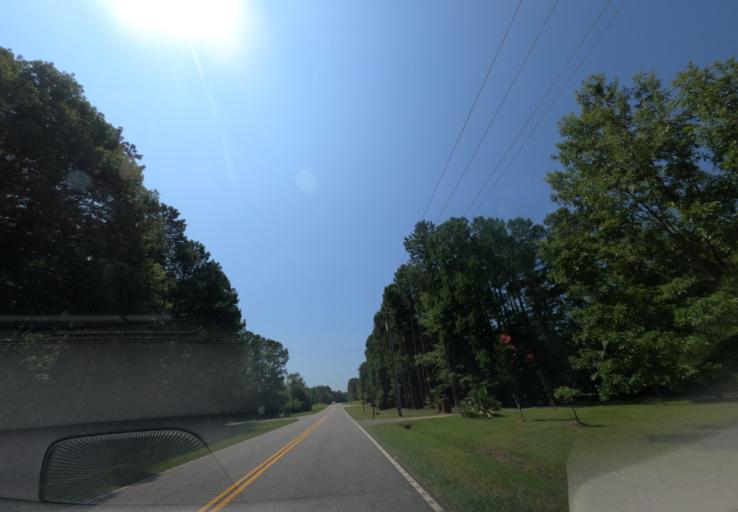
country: US
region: South Carolina
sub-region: Greenwood County
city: Greenwood
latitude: 34.1046
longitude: -82.1300
